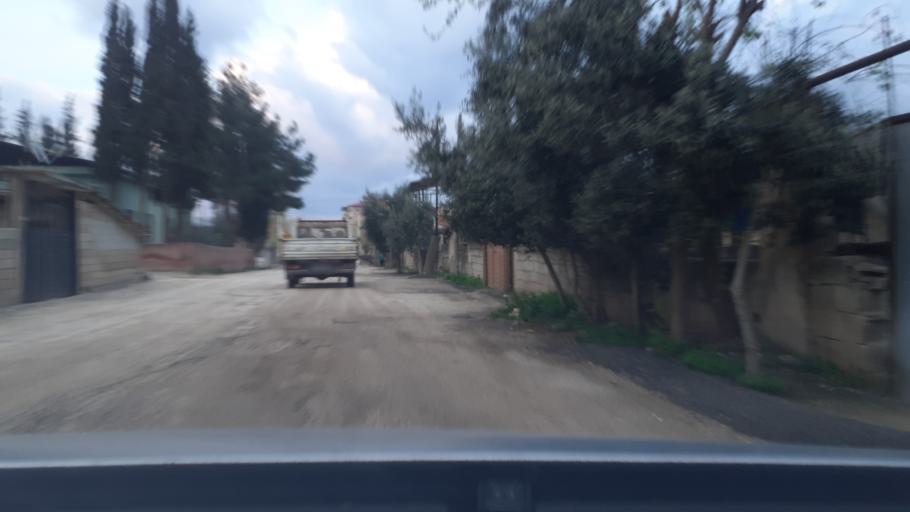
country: TR
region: Hatay
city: Kirikhan
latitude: 36.4833
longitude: 36.3503
